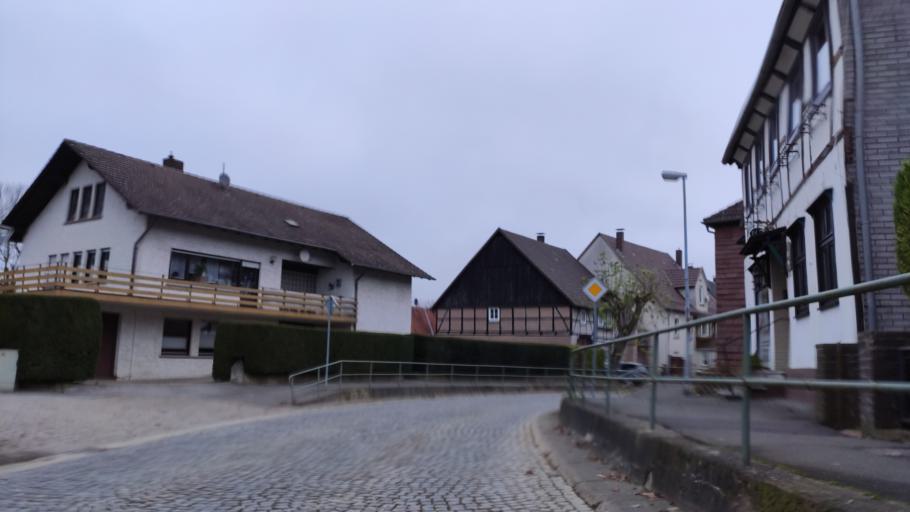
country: DE
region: North Rhine-Westphalia
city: Beverungen
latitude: 51.7059
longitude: 9.2890
